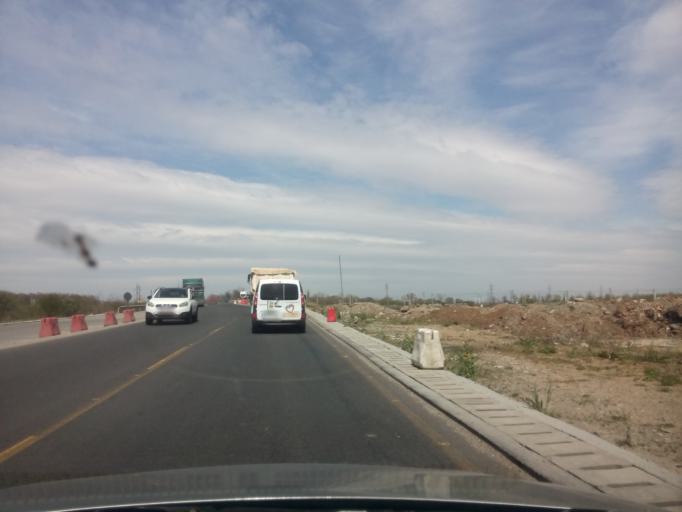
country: RO
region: Ilfov
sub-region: Comuna Pantelimon
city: Pantelimon
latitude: 44.4699
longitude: 26.2321
